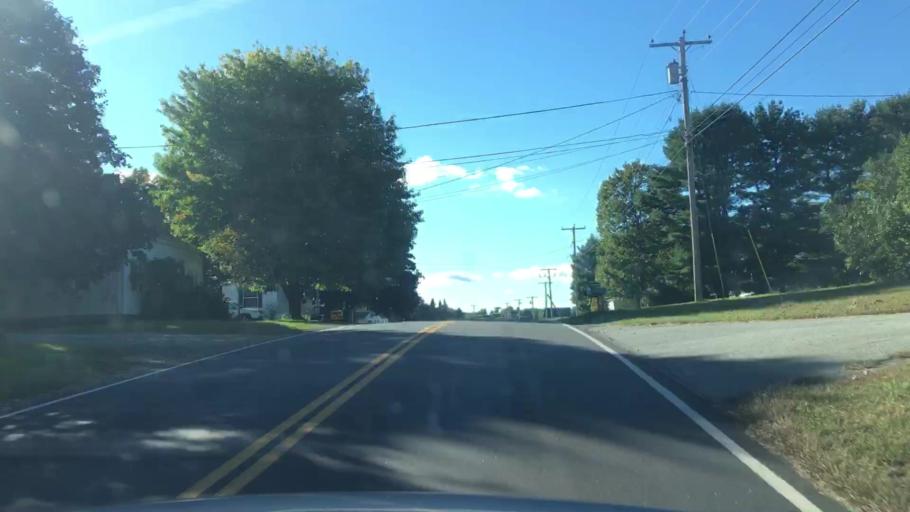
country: US
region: Maine
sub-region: Androscoggin County
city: Lisbon
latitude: 44.0755
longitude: -70.1109
